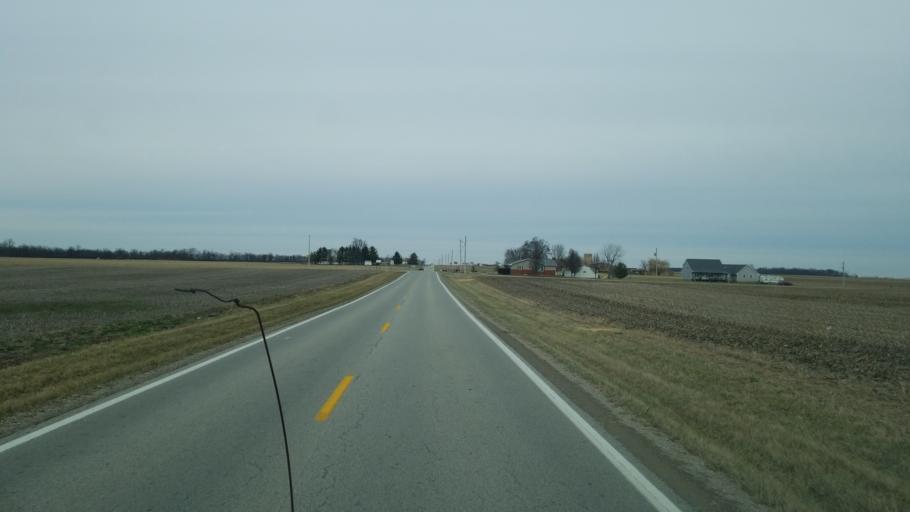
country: US
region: Ohio
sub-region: Ross County
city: Frankfort
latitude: 39.4536
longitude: -83.2119
